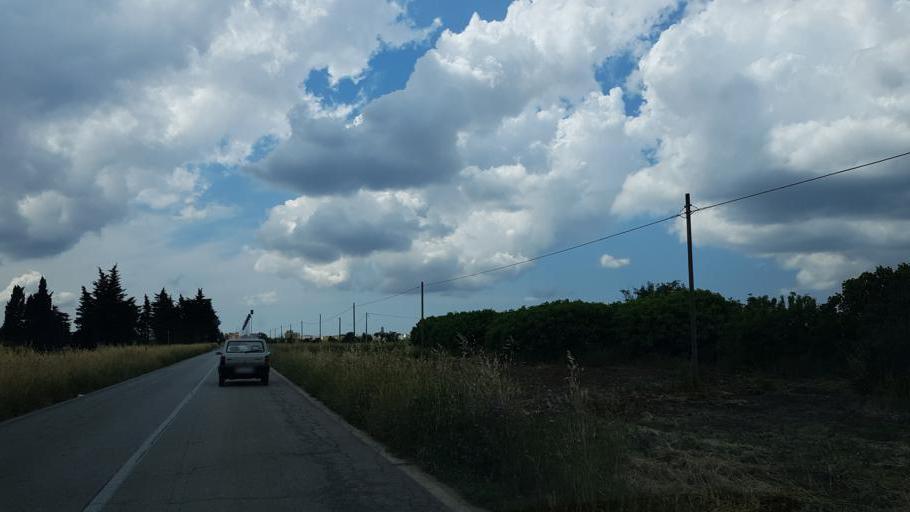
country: IT
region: Apulia
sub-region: Provincia di Brindisi
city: San Pancrazio Salentino
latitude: 40.4294
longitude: 17.8404
